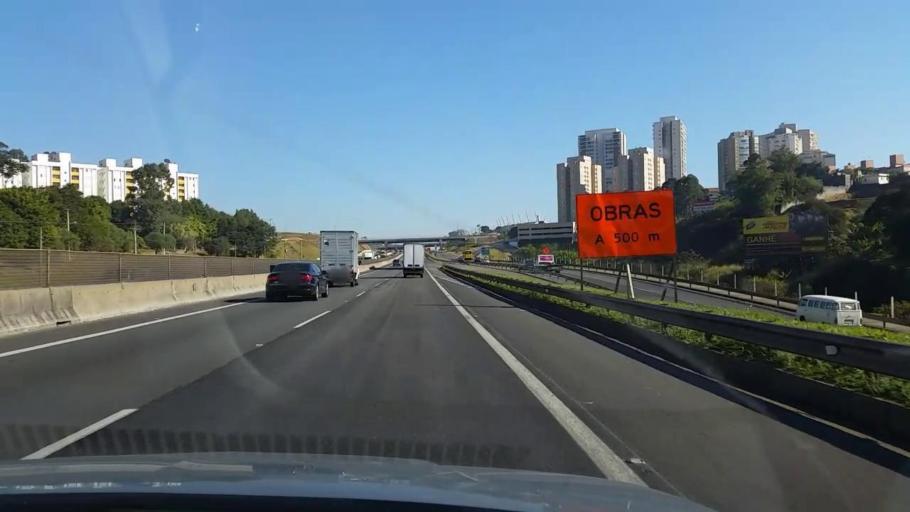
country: BR
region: Sao Paulo
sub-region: Jundiai
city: Jundiai
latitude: -23.2122
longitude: -46.8899
